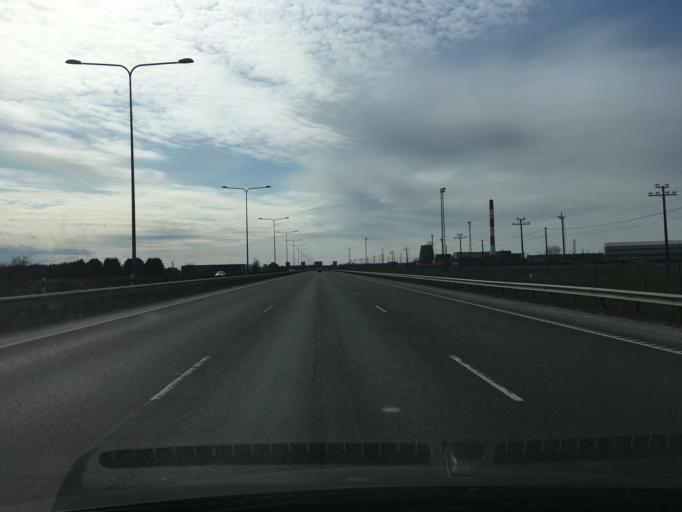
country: EE
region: Harju
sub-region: Joelaehtme vald
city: Loo
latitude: 59.4495
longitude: 24.9581
